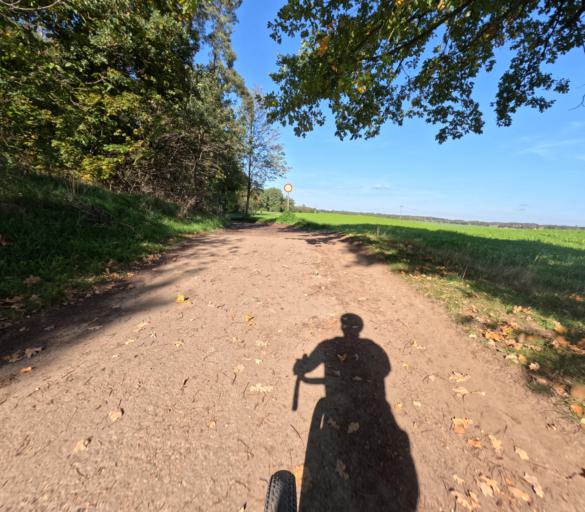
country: DE
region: Saxony
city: Moritzburg
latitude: 51.1698
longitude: 13.7177
